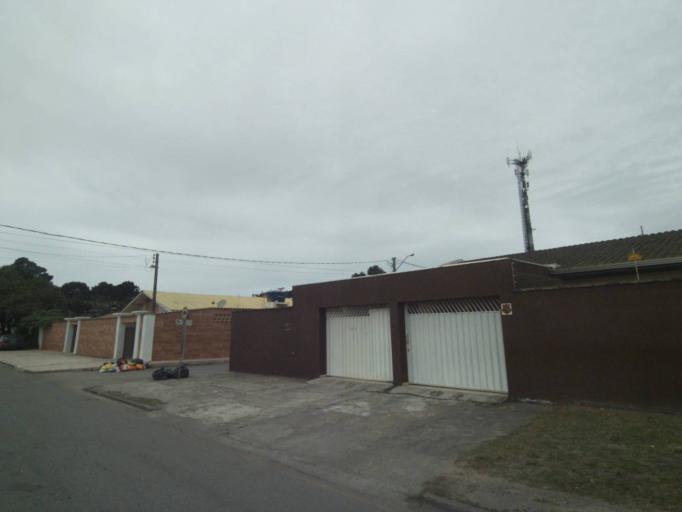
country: BR
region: Parana
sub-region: Paranagua
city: Paranagua
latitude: -25.5171
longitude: -48.5340
